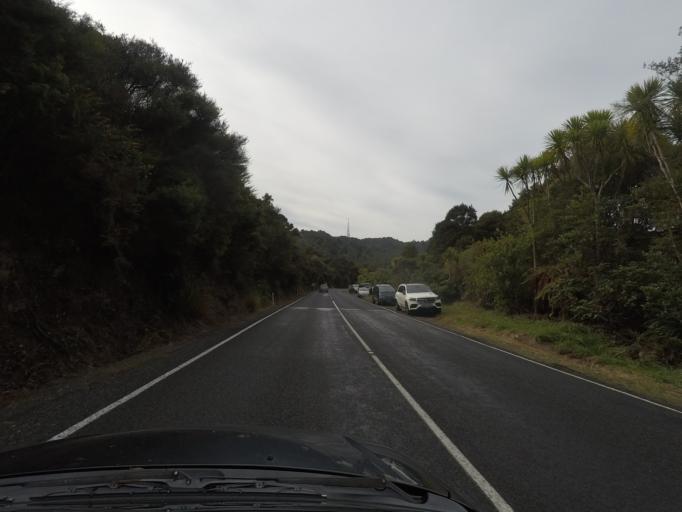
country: NZ
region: Auckland
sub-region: Auckland
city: Titirangi
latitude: -36.9379
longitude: 174.5551
